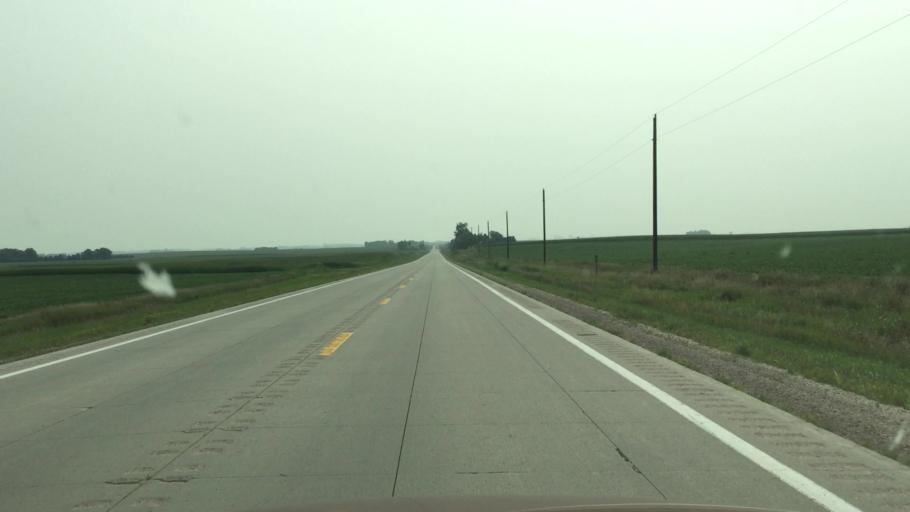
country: US
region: Iowa
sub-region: Osceola County
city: Sibley
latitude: 43.4327
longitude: -95.6581
